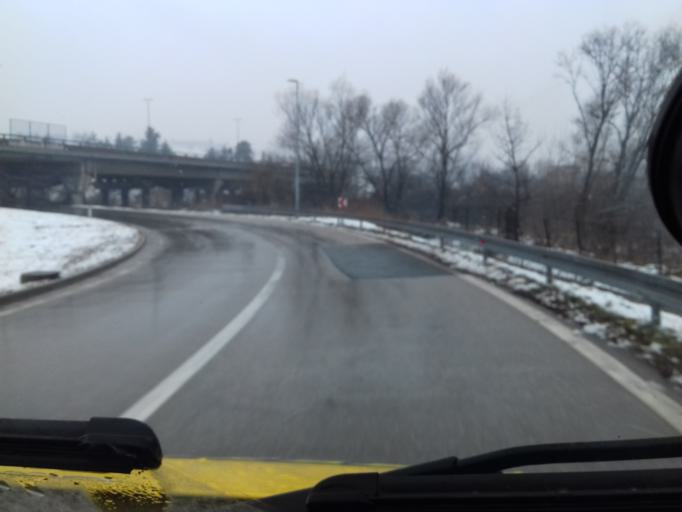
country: BA
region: Federation of Bosnia and Herzegovina
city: Gornje Mostre
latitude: 44.0056
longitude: 18.1673
